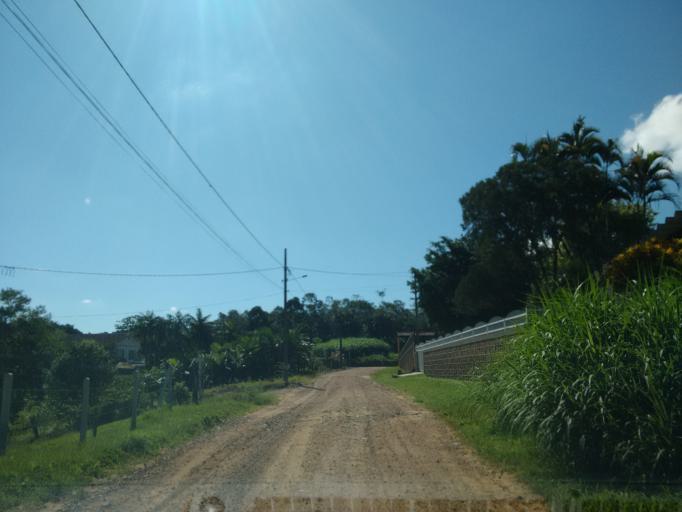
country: BR
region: Santa Catarina
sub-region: Indaial
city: Indaial
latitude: -26.9057
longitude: -49.1948
